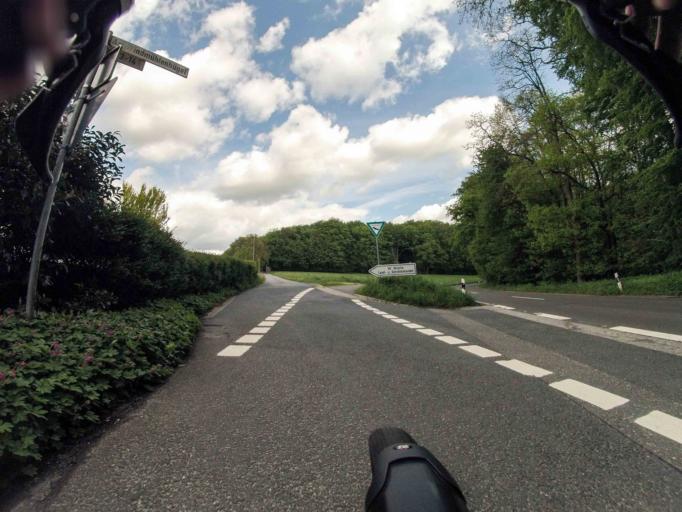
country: DE
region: North Rhine-Westphalia
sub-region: Regierungsbezirk Munster
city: Westerkappeln
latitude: 52.2938
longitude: 7.8622
